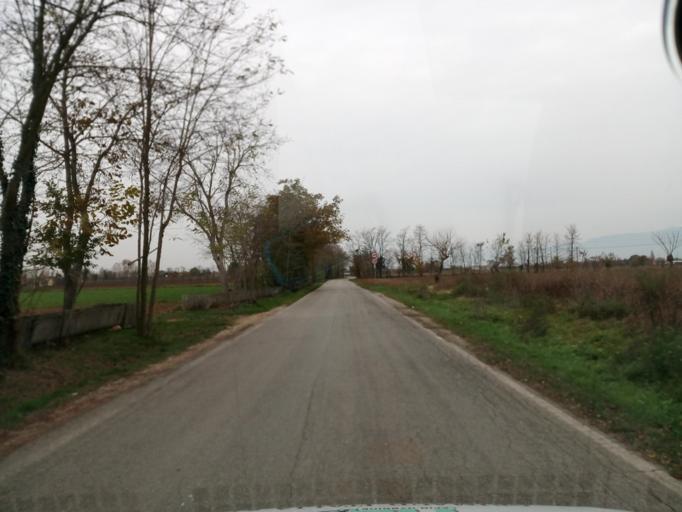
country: IT
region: Veneto
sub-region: Provincia di Treviso
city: Trevignano
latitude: 45.7269
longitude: 12.0431
